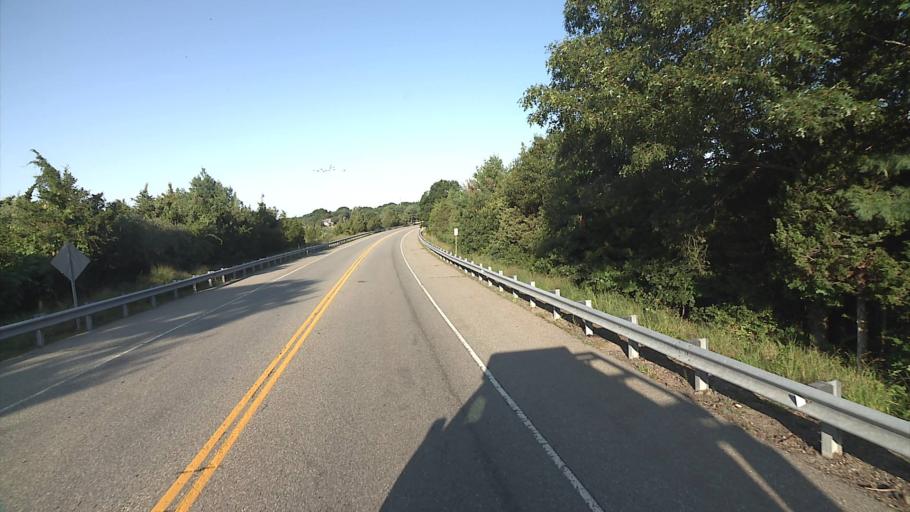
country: US
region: Connecticut
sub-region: New London County
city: Mystic
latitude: 41.3426
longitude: -71.9340
